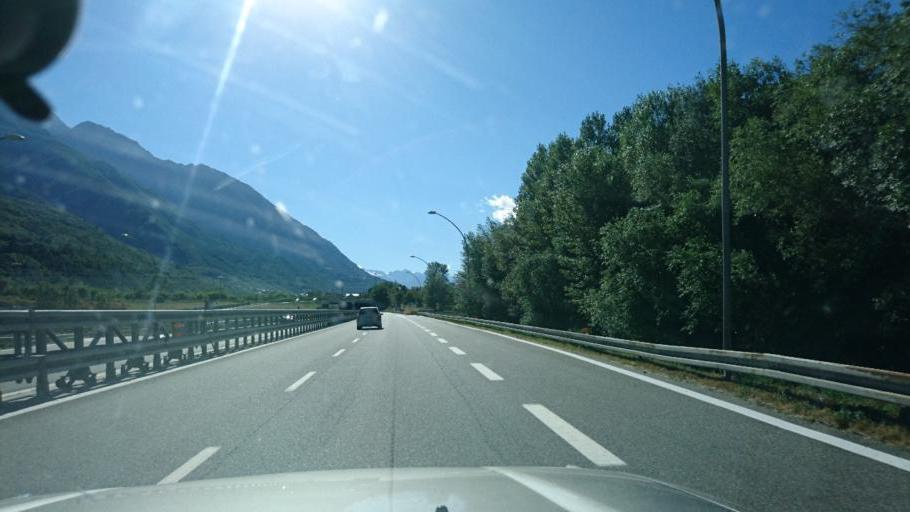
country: IT
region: Aosta Valley
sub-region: Valle d'Aosta
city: Nus
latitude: 45.7426
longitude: 7.4818
